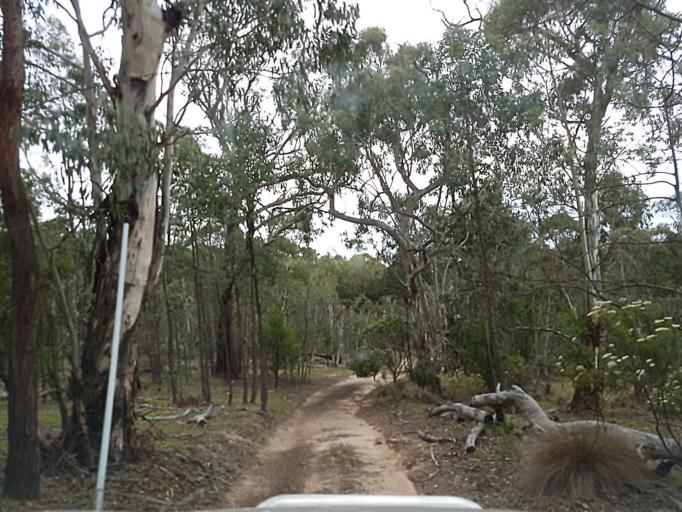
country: AU
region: New South Wales
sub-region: Snowy River
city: Jindabyne
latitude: -36.8836
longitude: 148.3382
